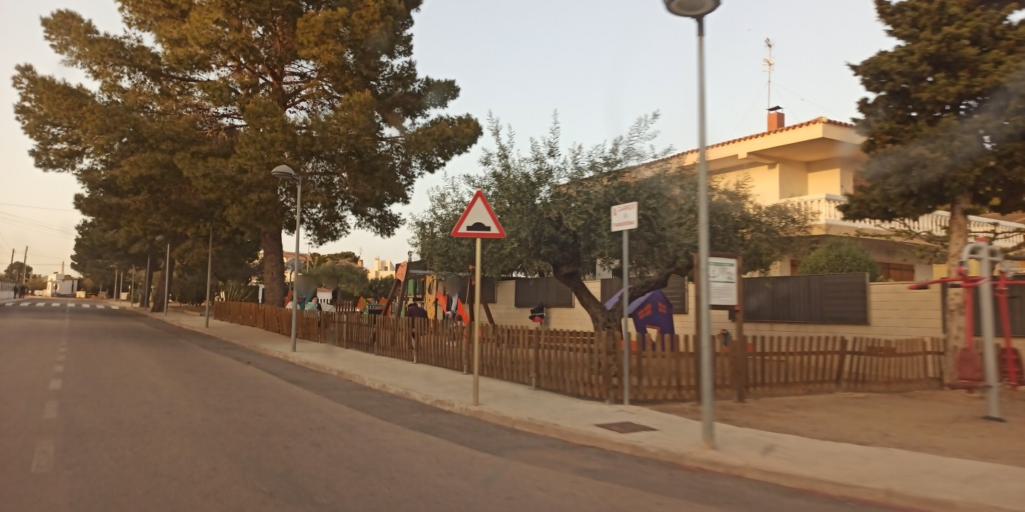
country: ES
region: Catalonia
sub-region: Provincia de Tarragona
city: L'Ampolla
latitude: 40.8230
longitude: 0.7293
